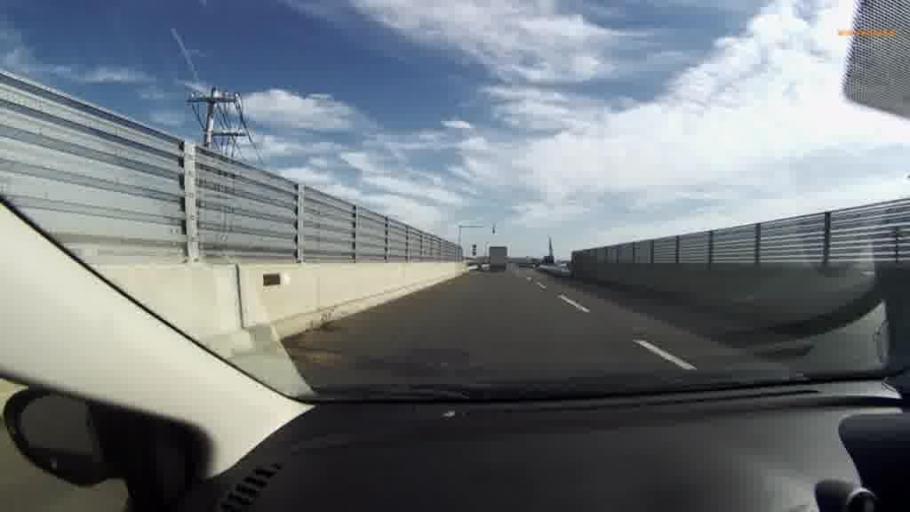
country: JP
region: Hokkaido
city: Kushiro
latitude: 43.0344
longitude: 144.3134
